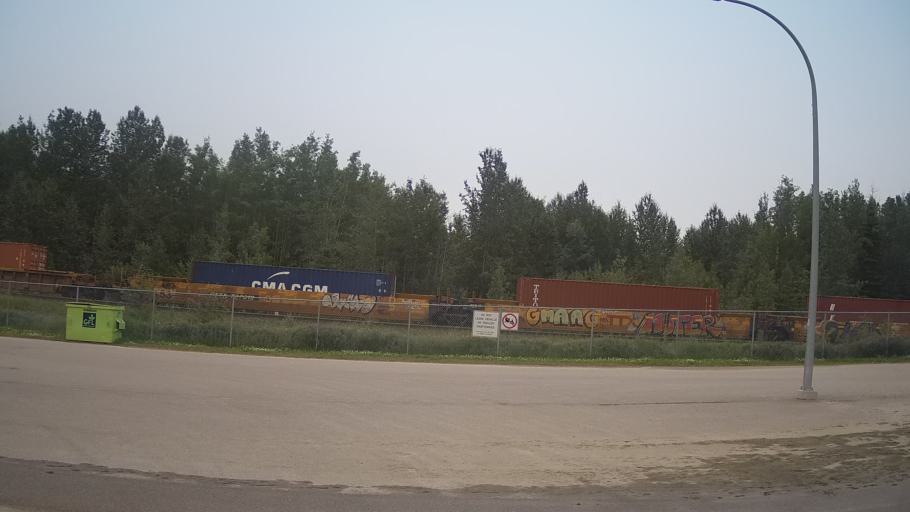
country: CA
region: Alberta
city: Edson
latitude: 53.5763
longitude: -116.4435
